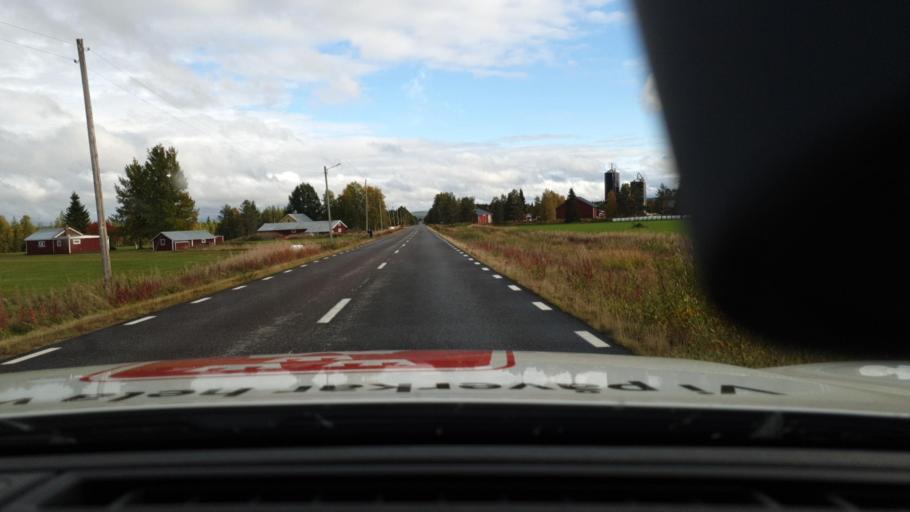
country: SE
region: Norrbotten
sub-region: Overkalix Kommun
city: OEverkalix
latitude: 66.9543
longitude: 22.7025
